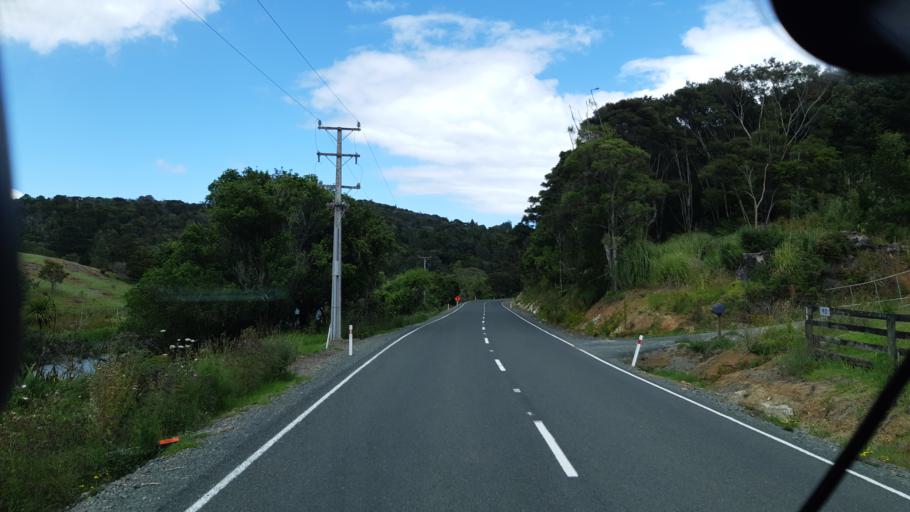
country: NZ
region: Northland
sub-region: Far North District
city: Taipa
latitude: -35.2419
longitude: 173.5381
